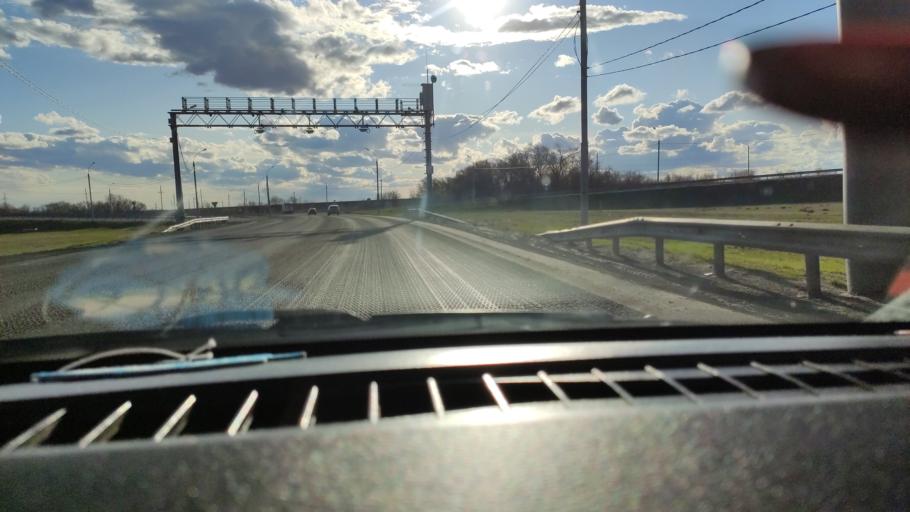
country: RU
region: Saratov
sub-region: Saratovskiy Rayon
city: Saratov
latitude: 51.7726
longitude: 46.0856
